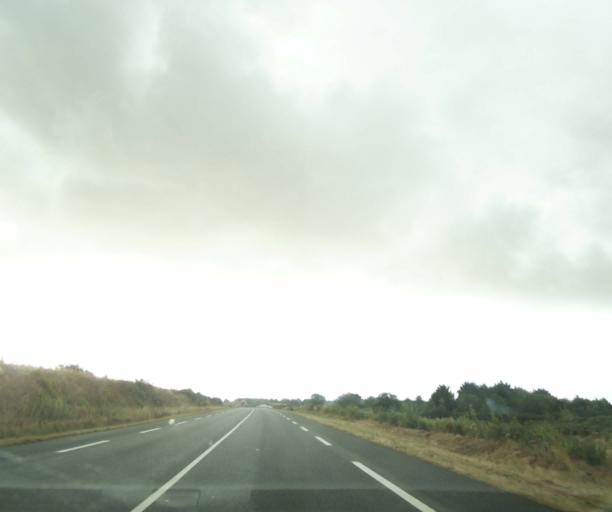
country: FR
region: Pays de la Loire
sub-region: Departement de la Vendee
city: Saint-Hilaire-de-Talmont
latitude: 46.4638
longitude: -1.6400
